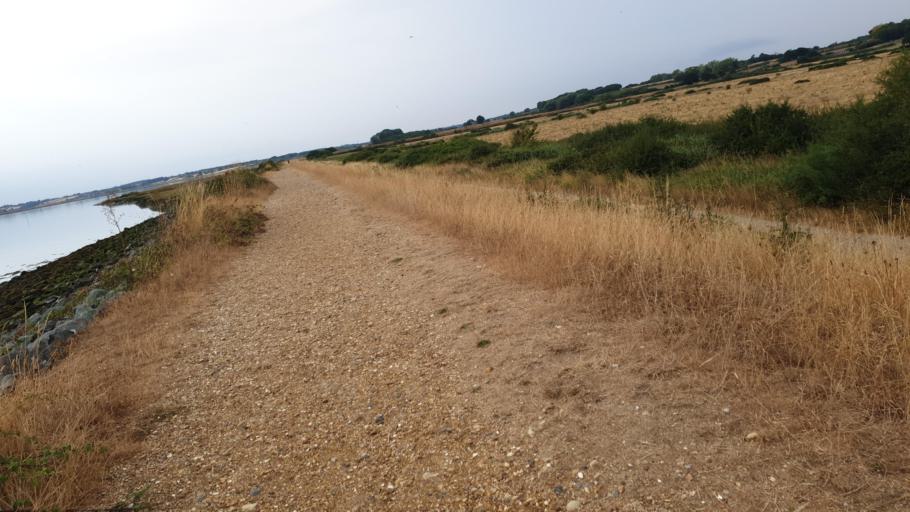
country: GB
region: England
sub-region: Essex
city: Brightlingsea
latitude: 51.8109
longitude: 1.0033
